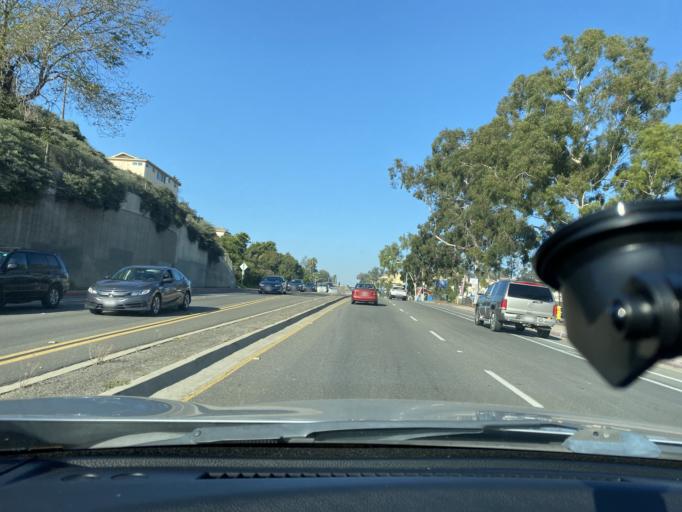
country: US
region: California
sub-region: San Diego County
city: Lemon Grove
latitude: 32.7468
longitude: -117.0795
